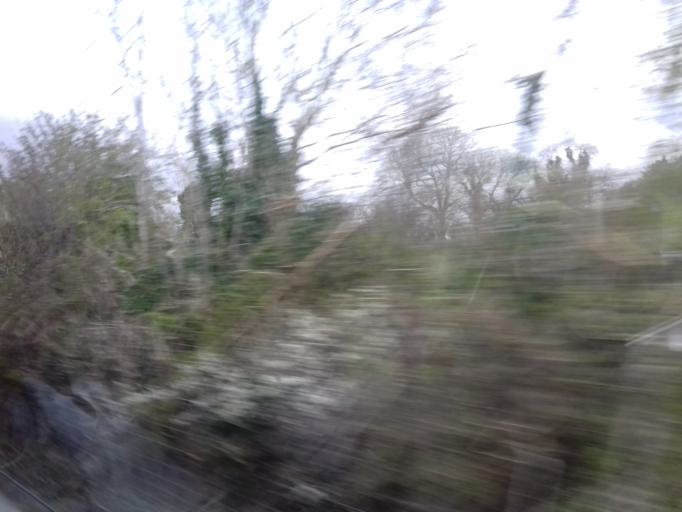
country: IE
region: Leinster
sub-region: An Longfort
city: Longford
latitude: 53.7547
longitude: -7.8265
